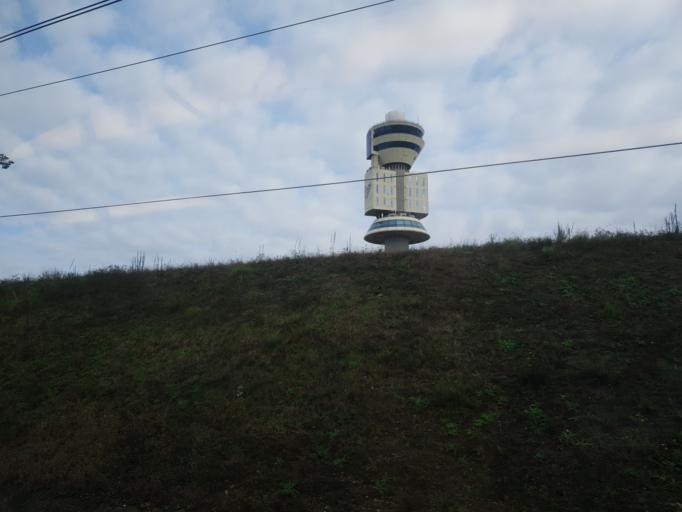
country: IT
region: Lombardy
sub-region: Provincia di Varese
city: Vizzola Ticino
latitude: 45.6197
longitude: 8.7134
